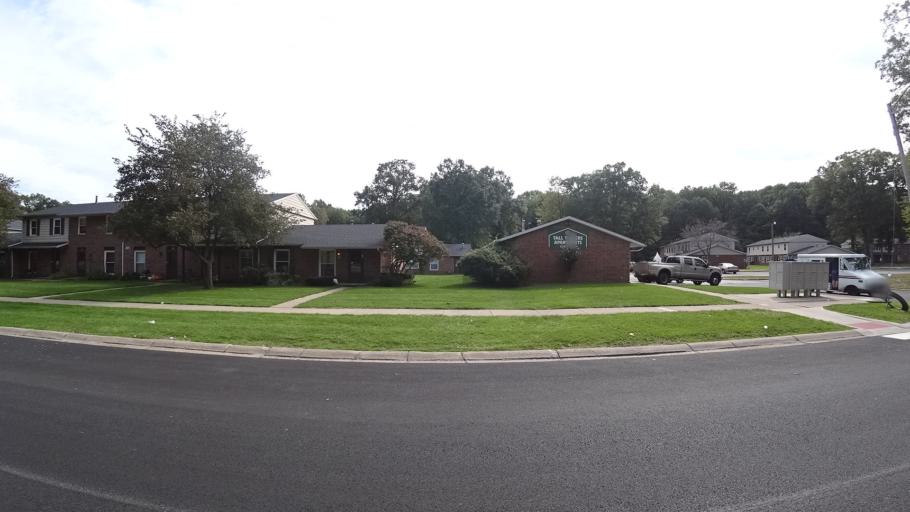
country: US
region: Indiana
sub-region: LaPorte County
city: Long Beach
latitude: 41.7177
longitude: -86.8342
